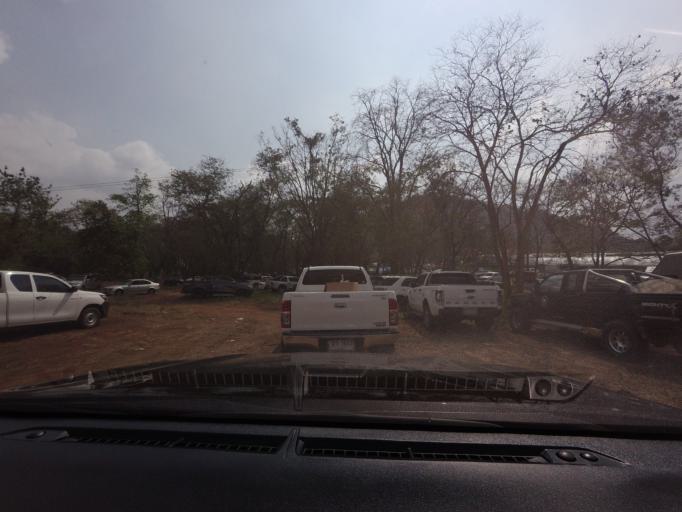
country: TH
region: Sara Buri
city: Muak Lek
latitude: 14.6344
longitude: 101.1928
